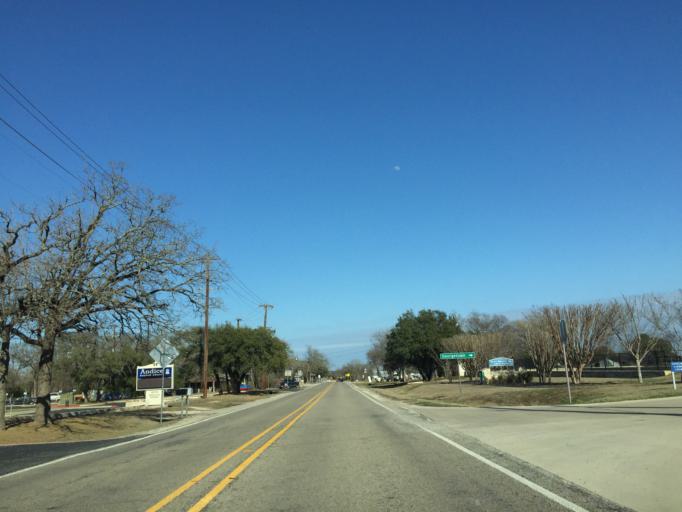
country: US
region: Texas
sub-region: Williamson County
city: Florence
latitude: 30.7818
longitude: -97.8546
